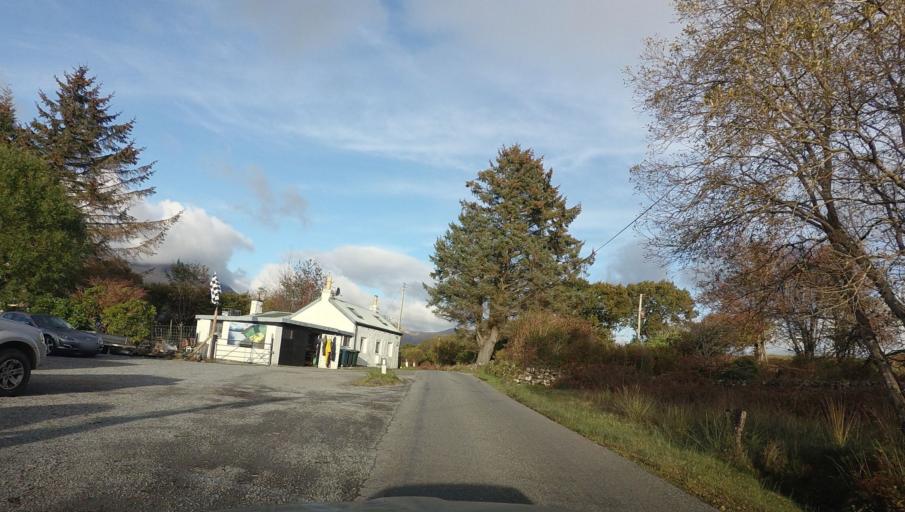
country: GB
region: Scotland
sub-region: Argyll and Bute
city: Isle Of Mull
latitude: 56.3602
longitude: -6.0431
